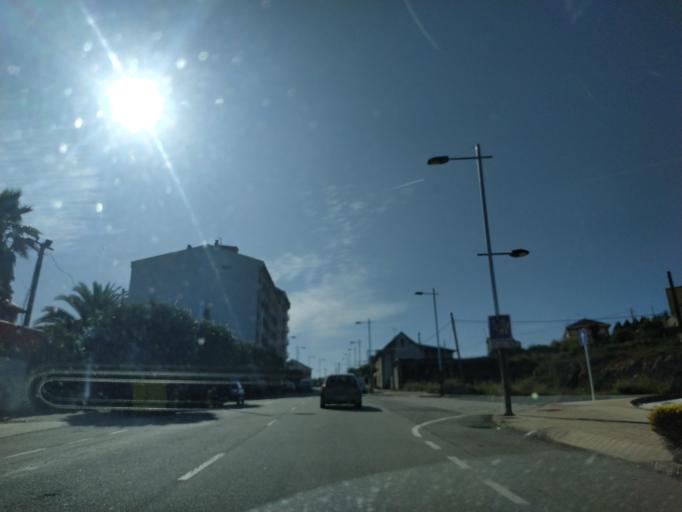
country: ES
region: Galicia
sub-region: Provincia da Coruna
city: Cerceda
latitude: 43.1883
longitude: -8.4762
